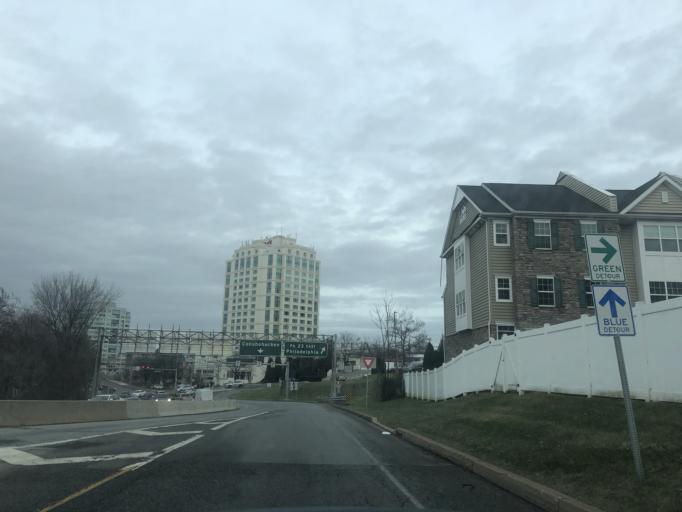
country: US
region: Pennsylvania
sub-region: Montgomery County
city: West Conshohocken
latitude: 40.0679
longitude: -75.3126
